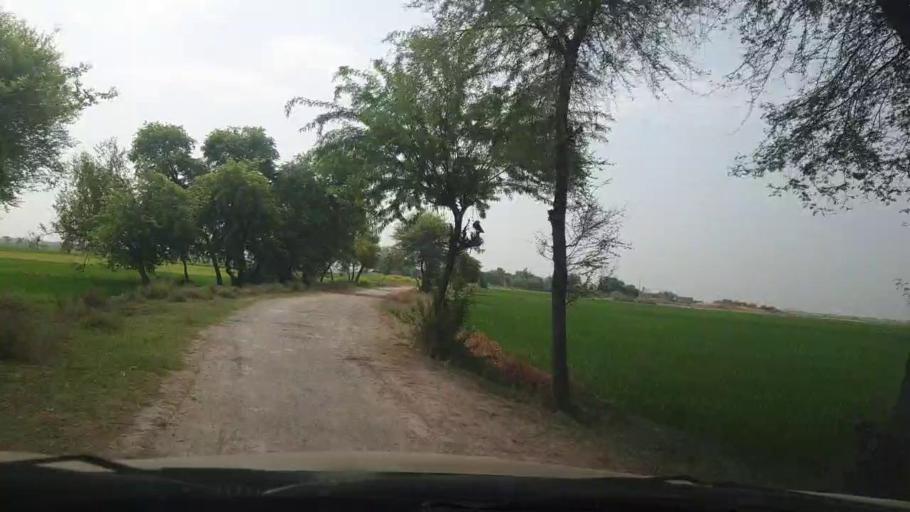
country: PK
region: Sindh
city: Larkana
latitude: 27.6838
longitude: 68.2019
